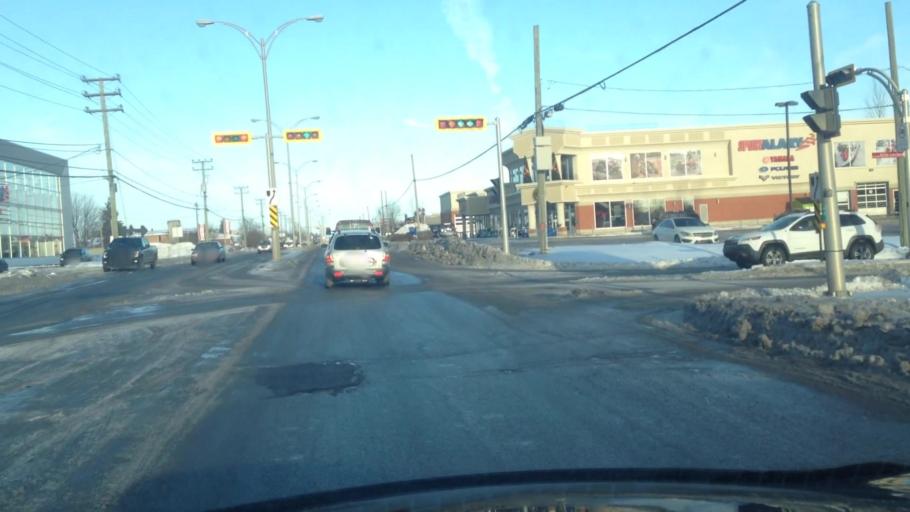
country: CA
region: Quebec
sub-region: Laurentides
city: Saint-Jerome
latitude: 45.7679
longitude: -73.9764
